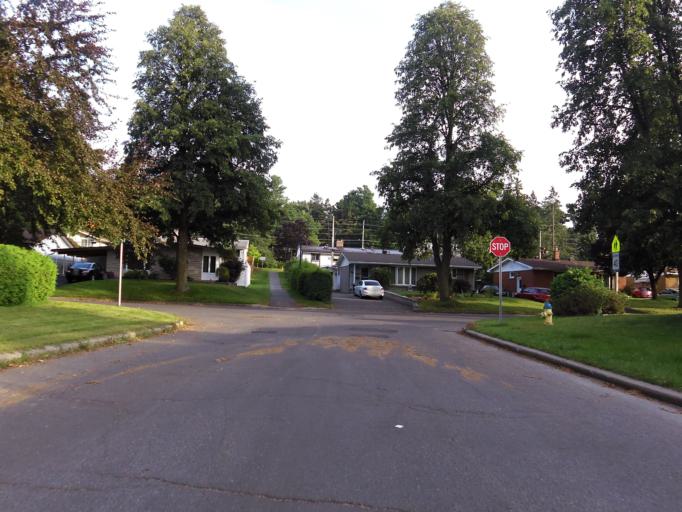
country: CA
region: Ontario
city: Bells Corners
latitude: 45.3443
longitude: -75.7829
